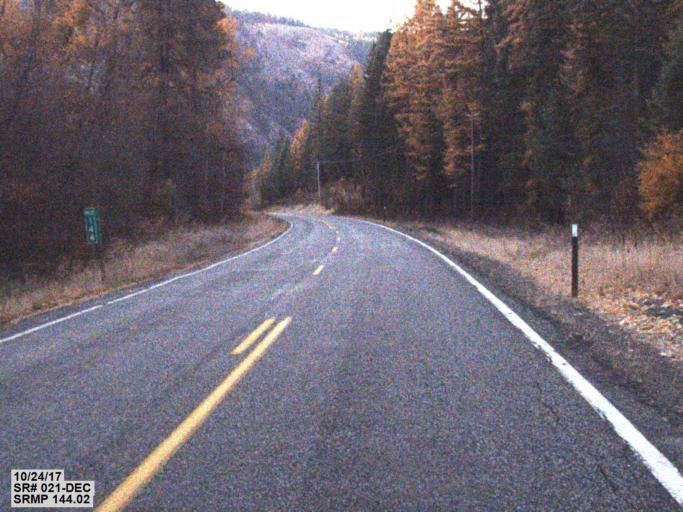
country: US
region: Washington
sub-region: Ferry County
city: Republic
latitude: 48.4372
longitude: -118.7379
